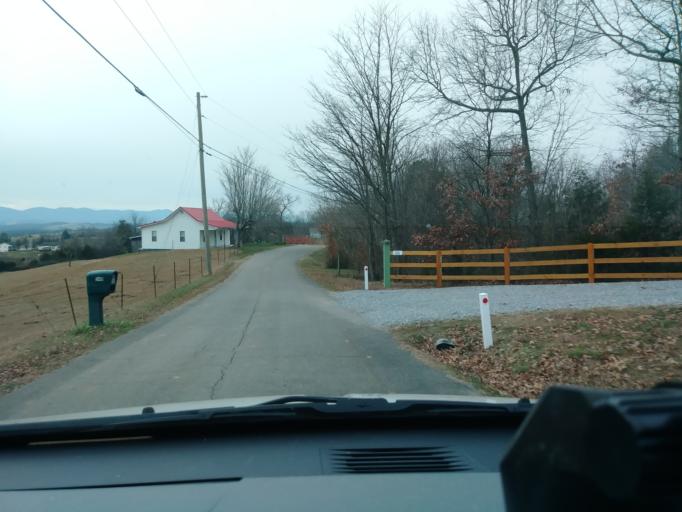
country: US
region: Tennessee
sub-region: Greene County
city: Greeneville
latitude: 36.0980
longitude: -82.8913
